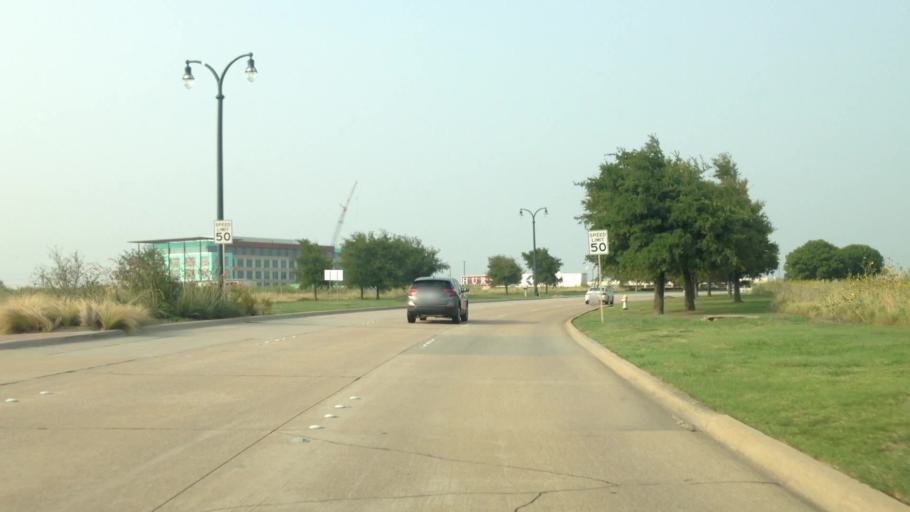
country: US
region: Texas
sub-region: Denton County
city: The Colony
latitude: 33.0463
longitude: -96.8735
